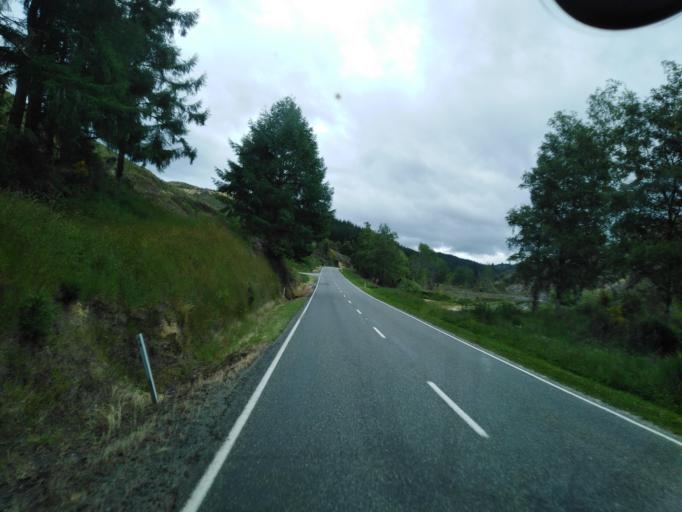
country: NZ
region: Tasman
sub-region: Tasman District
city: Wakefield
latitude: -41.6202
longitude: 172.7528
